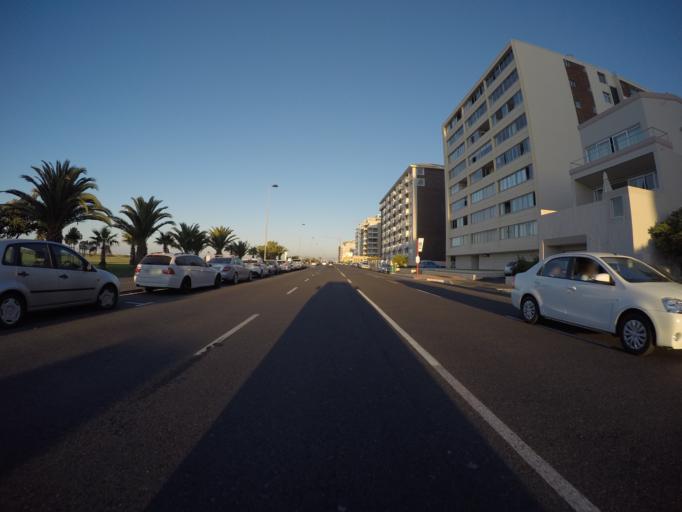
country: ZA
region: Western Cape
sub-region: City of Cape Town
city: Cape Town
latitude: -33.9011
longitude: 18.4013
